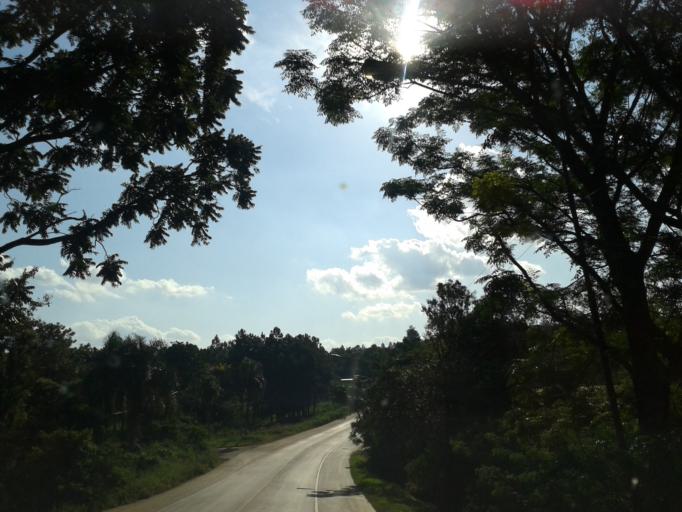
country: AR
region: Misiones
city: Guarani
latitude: -27.4945
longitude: -55.1638
